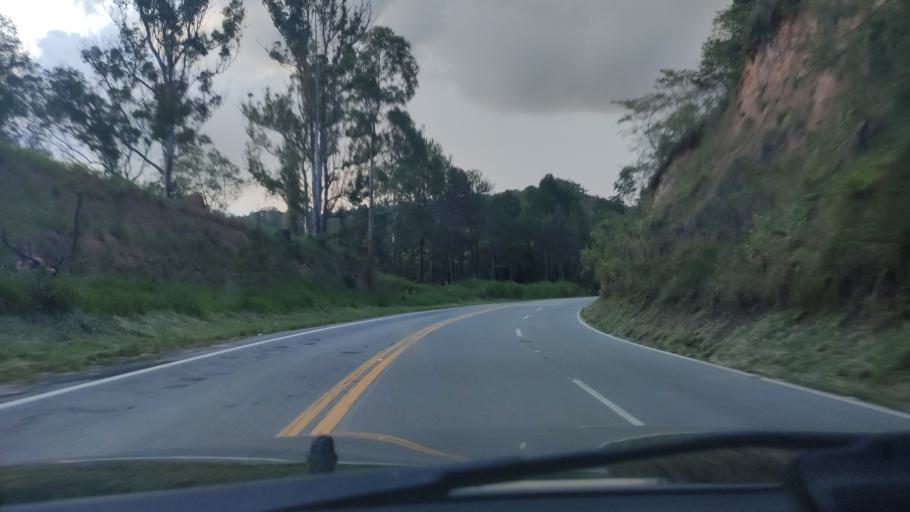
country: BR
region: Sao Paulo
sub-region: Braganca Paulista
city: Braganca Paulista
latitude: -22.8364
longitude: -46.5567
